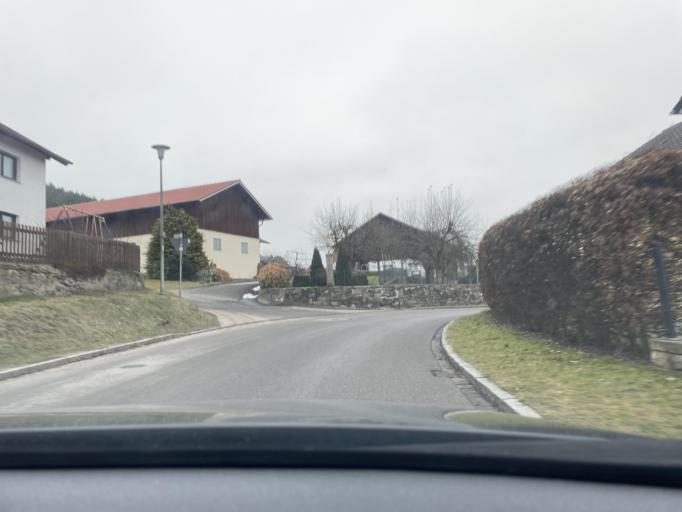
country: DE
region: Bavaria
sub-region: Upper Palatinate
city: Cham
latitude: 49.1932
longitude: 12.6894
